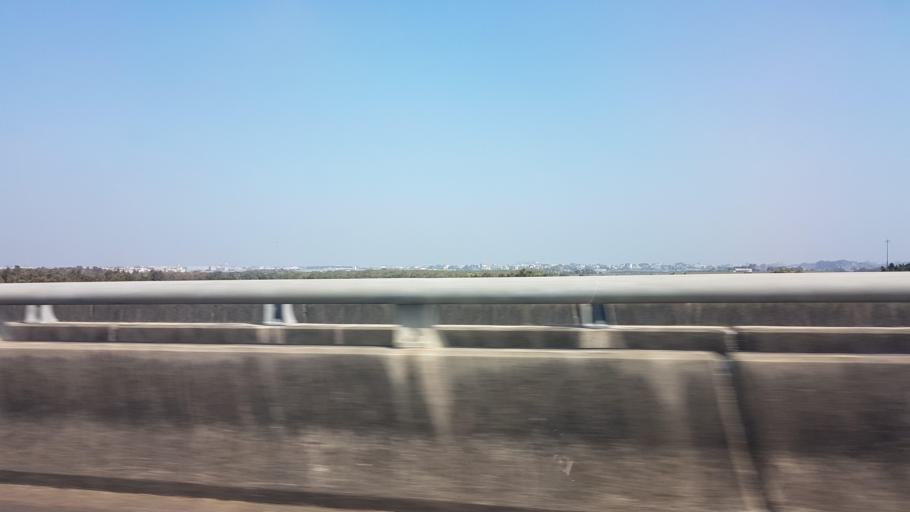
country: TW
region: Taiwan
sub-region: Chiayi
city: Taibao
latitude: 23.4250
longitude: 120.3549
